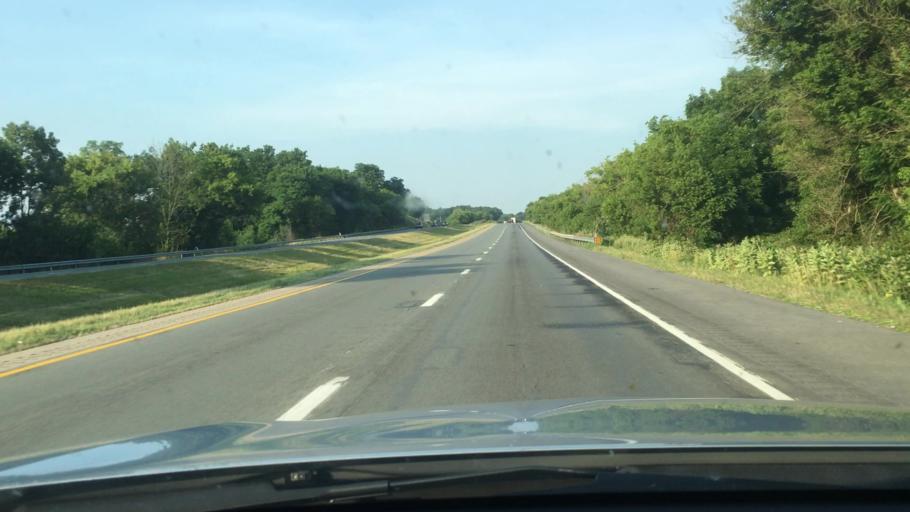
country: US
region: Pennsylvania
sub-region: Cumberland County
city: Shippensburg
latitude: 40.0742
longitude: -77.4539
